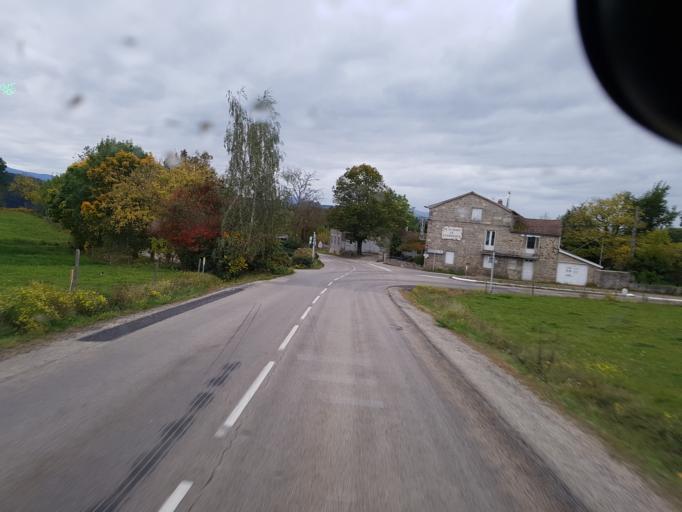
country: FR
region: Auvergne
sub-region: Departement de la Haute-Loire
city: Sainte-Sigolene
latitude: 45.2323
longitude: 4.2100
